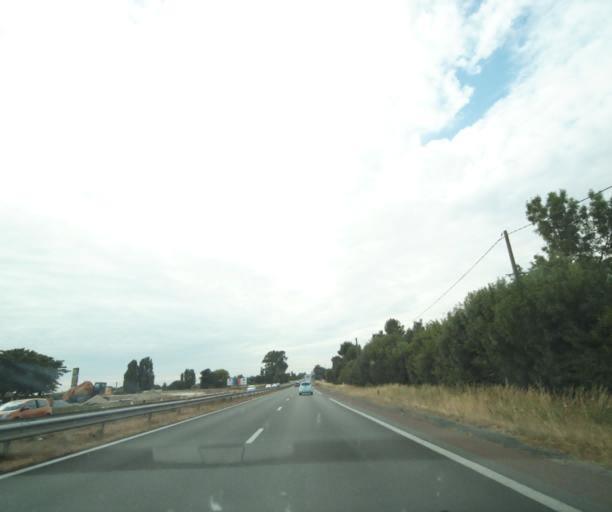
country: FR
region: Poitou-Charentes
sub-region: Departement de la Charente-Maritime
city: Angoulins
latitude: 46.1116
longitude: -1.1018
